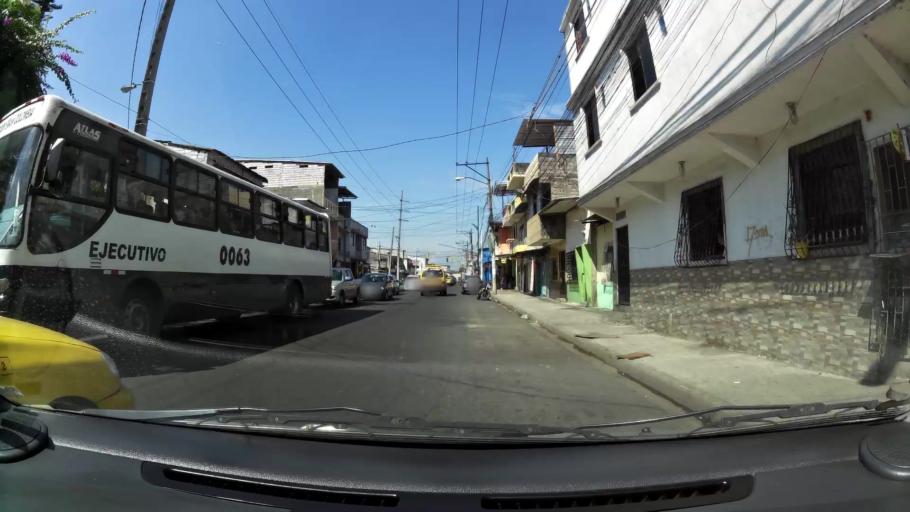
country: EC
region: Guayas
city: Guayaquil
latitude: -2.2103
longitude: -79.9085
